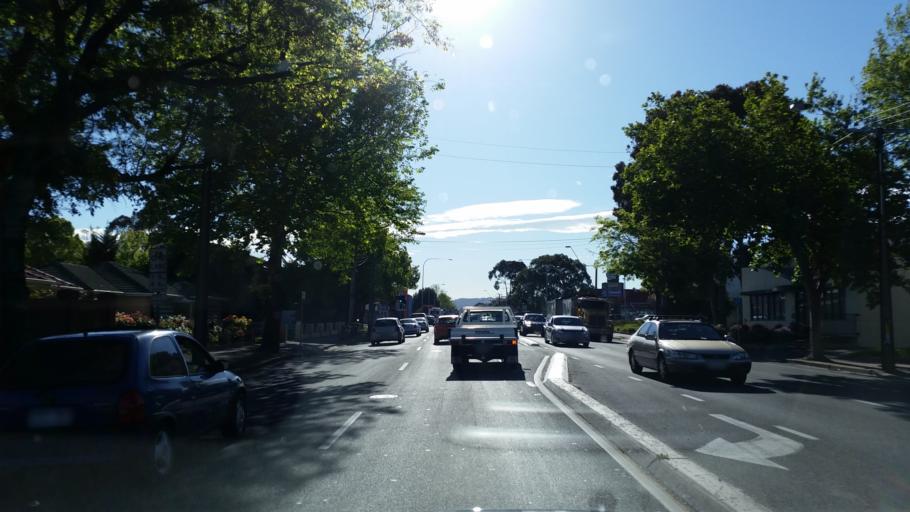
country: AU
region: South Australia
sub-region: Prospect
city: Prospect
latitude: -34.8737
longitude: 138.6007
